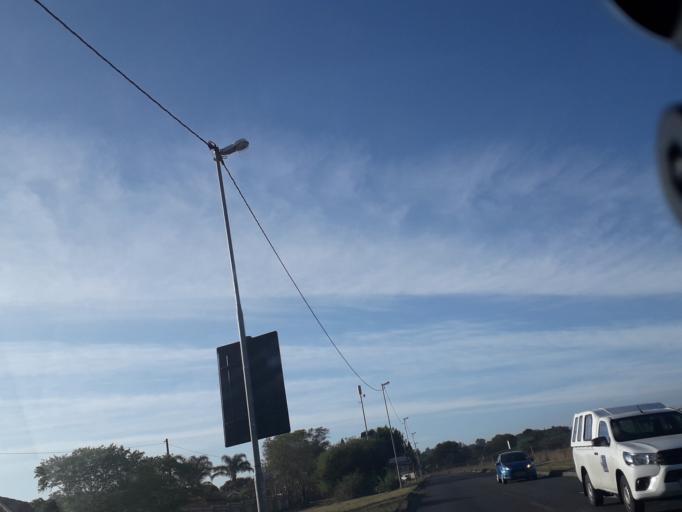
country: ZA
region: Gauteng
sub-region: City of Johannesburg Metropolitan Municipality
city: Roodepoort
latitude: -26.0989
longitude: 27.9173
